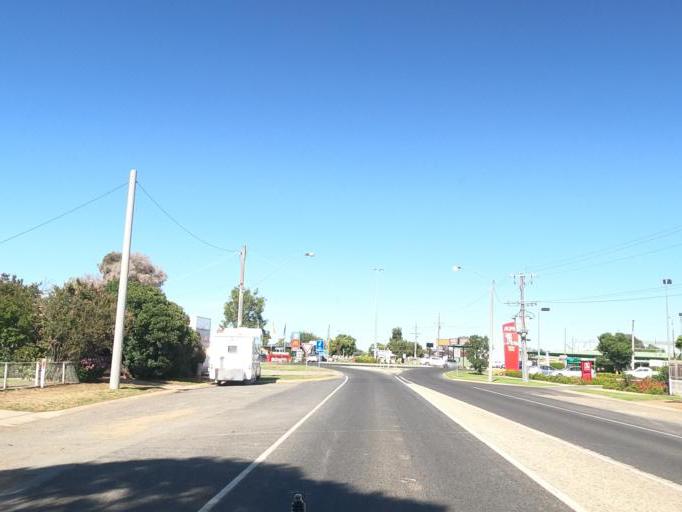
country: AU
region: Victoria
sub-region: Moira
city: Yarrawonga
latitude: -36.0174
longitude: 146.0057
